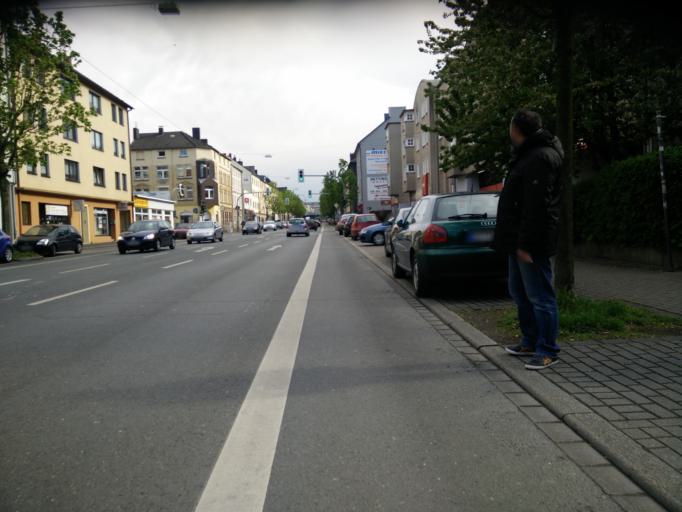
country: DE
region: North Rhine-Westphalia
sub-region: Regierungsbezirk Arnsberg
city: Bochum
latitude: 51.4927
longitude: 7.2130
